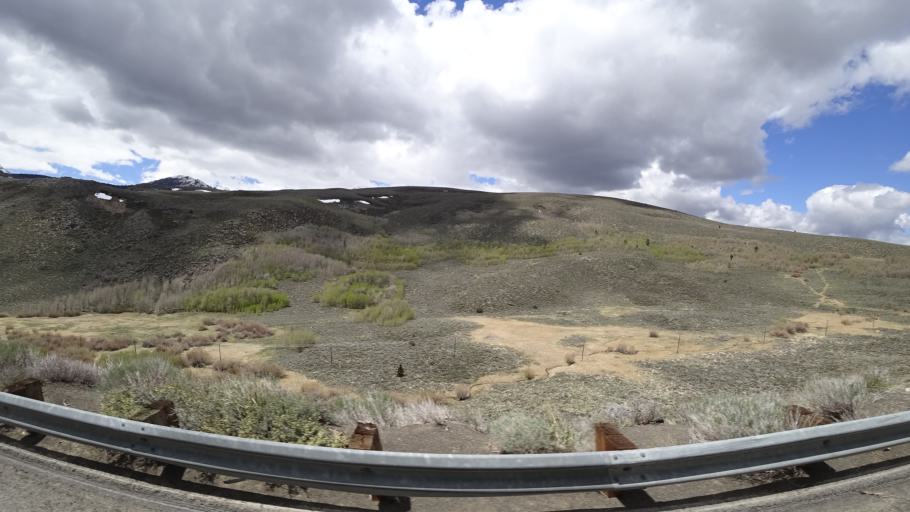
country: US
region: California
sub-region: Mono County
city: Bridgeport
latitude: 38.0789
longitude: -119.1785
